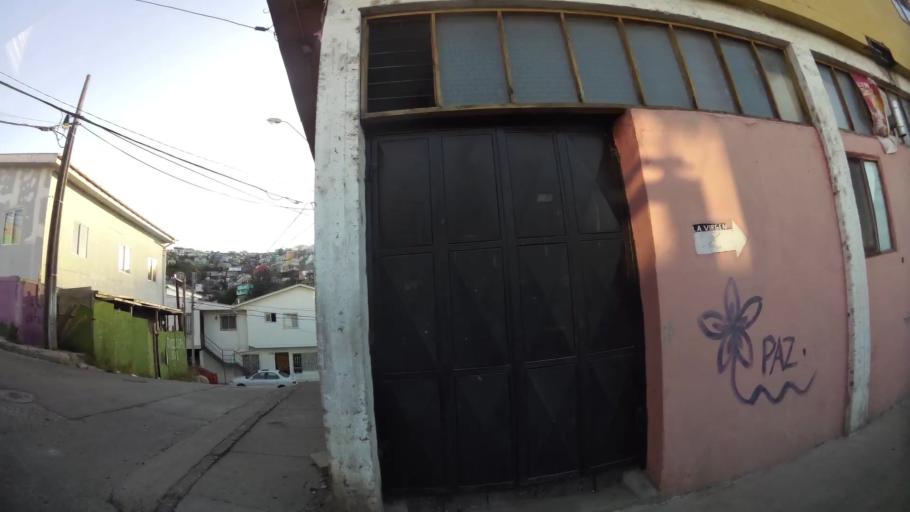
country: CL
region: Valparaiso
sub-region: Provincia de Valparaiso
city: Valparaiso
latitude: -33.0574
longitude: -71.6049
